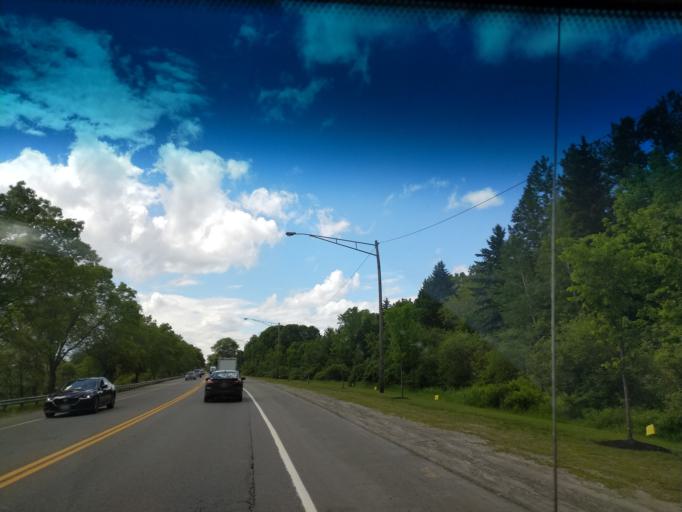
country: US
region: Maine
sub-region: Cumberland County
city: Westbrook
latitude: 43.6794
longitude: -70.3750
